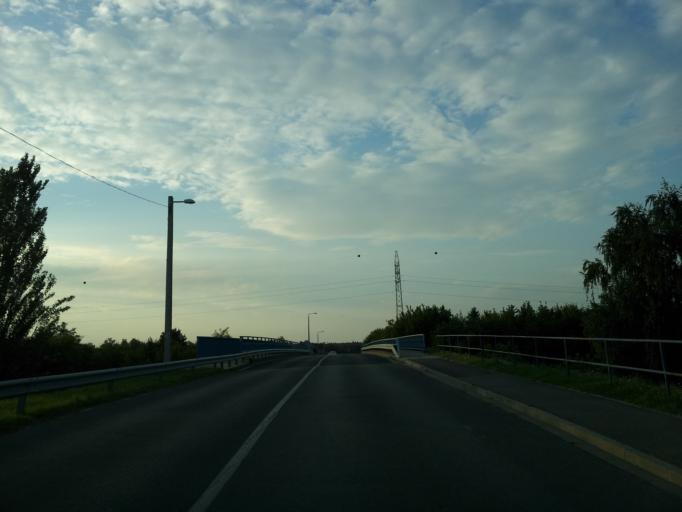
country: HU
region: Somogy
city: Siofok
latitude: 46.8917
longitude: 18.0480
